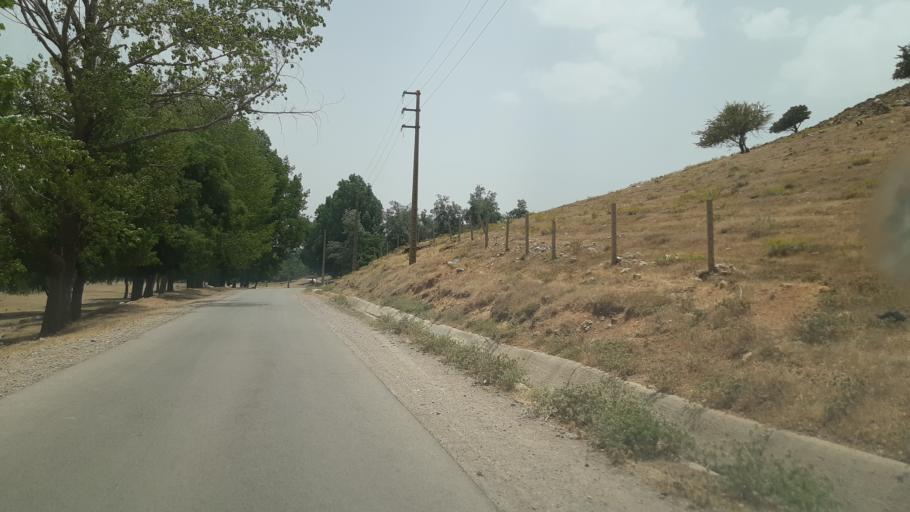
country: MA
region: Meknes-Tafilalet
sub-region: Ifrane
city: Ifrane
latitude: 33.6513
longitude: -5.0400
